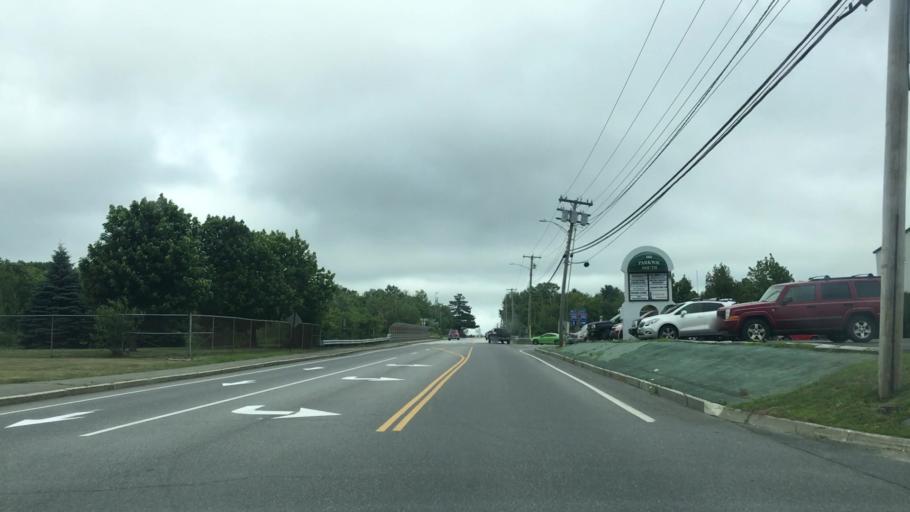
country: US
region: Maine
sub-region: Penobscot County
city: Brewer
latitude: 44.7800
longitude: -68.7605
